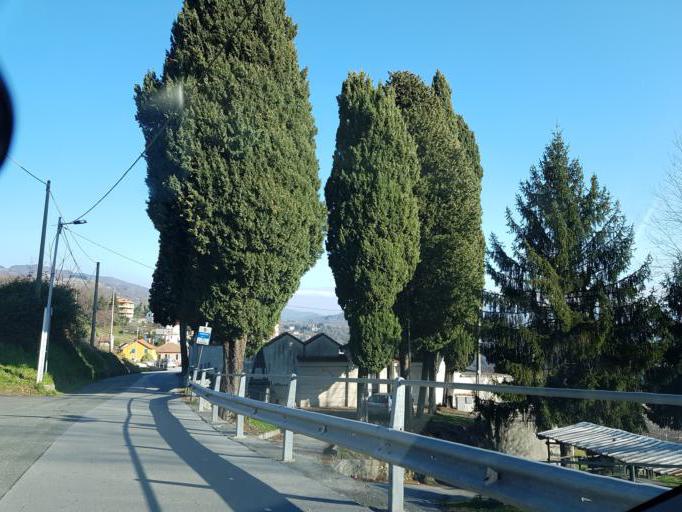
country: IT
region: Liguria
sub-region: Provincia di Genova
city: Campomorone
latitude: 44.5060
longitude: 8.8723
